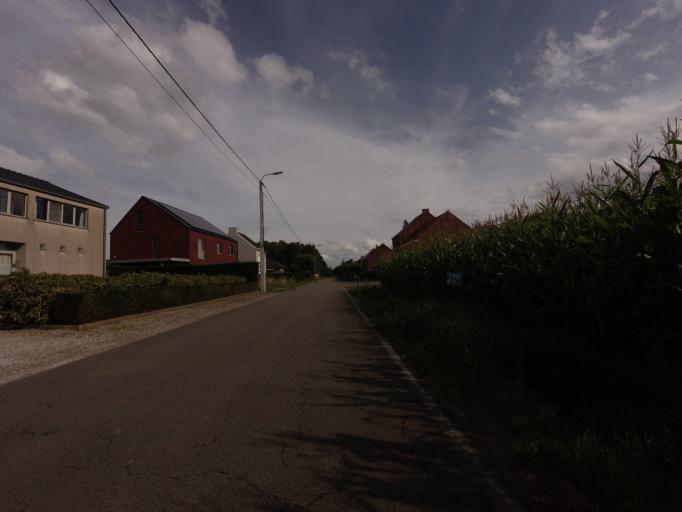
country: BE
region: Flanders
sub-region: Provincie Vlaams-Brabant
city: Kapelle-op-den-Bos
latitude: 51.0254
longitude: 4.3736
